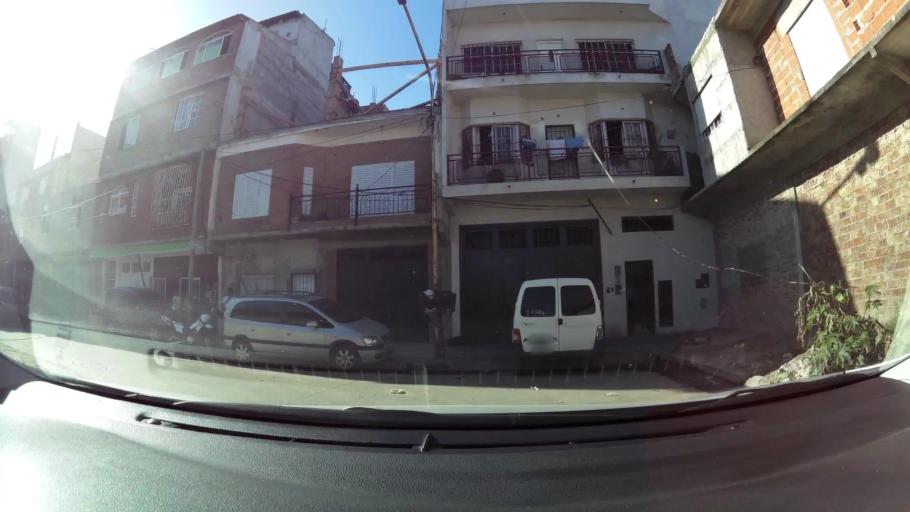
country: AR
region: Buenos Aires F.D.
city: Villa Lugano
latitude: -34.7021
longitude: -58.4809
